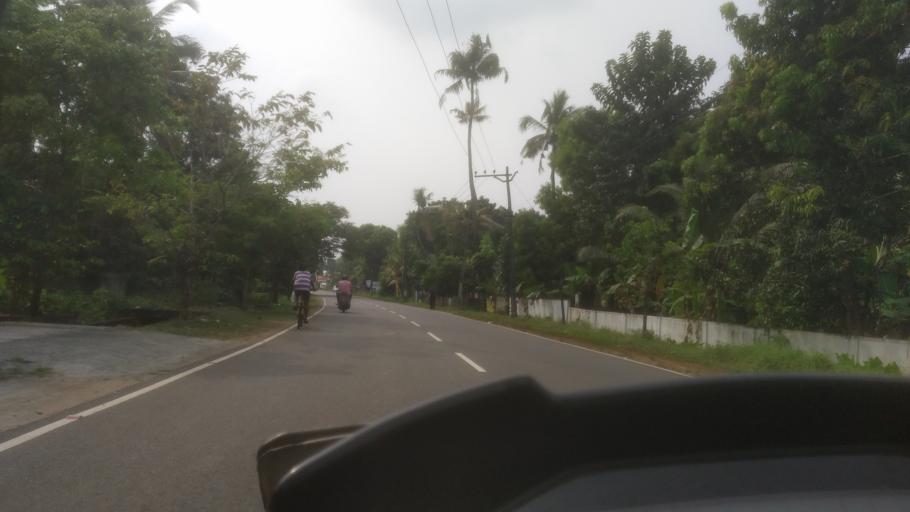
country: IN
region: Kerala
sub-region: Ernakulam
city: Angamali
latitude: 10.1641
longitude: 76.4041
